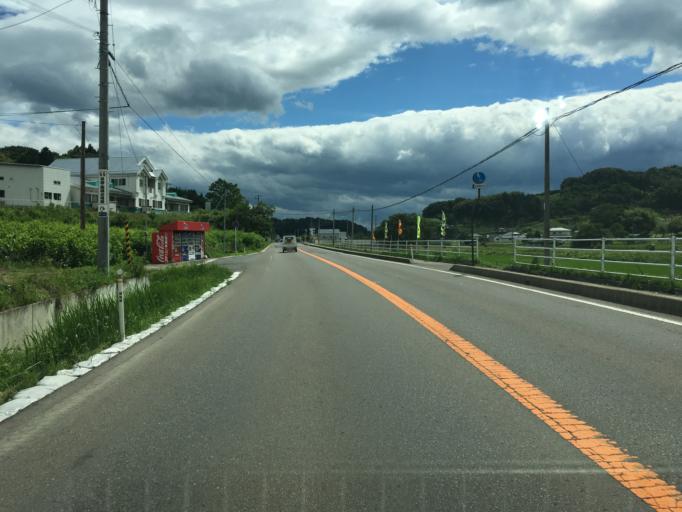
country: JP
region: Fukushima
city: Fukushima-shi
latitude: 37.6732
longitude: 140.5598
